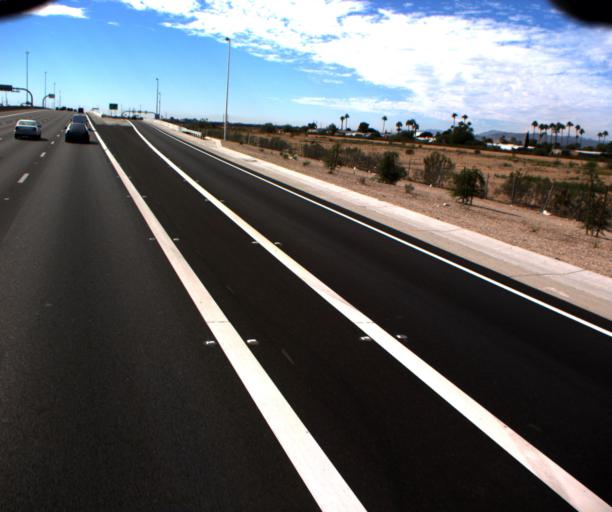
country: US
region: Arizona
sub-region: Maricopa County
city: Tempe
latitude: 33.4555
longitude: -111.8901
